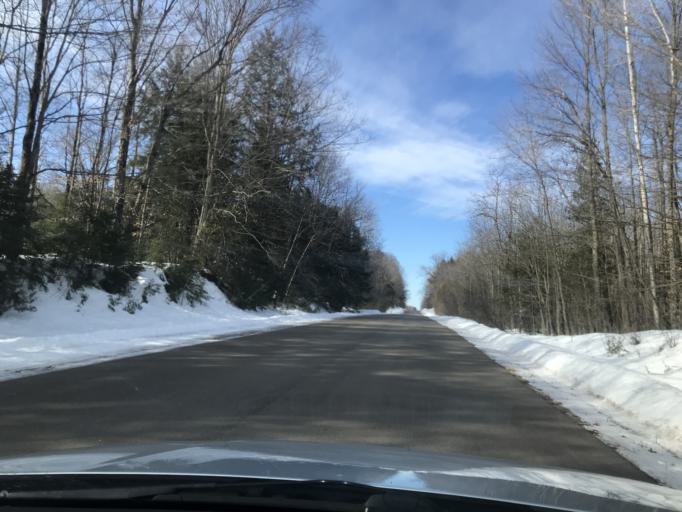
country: US
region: Wisconsin
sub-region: Oconto County
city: Gillett
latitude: 44.9616
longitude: -88.2775
